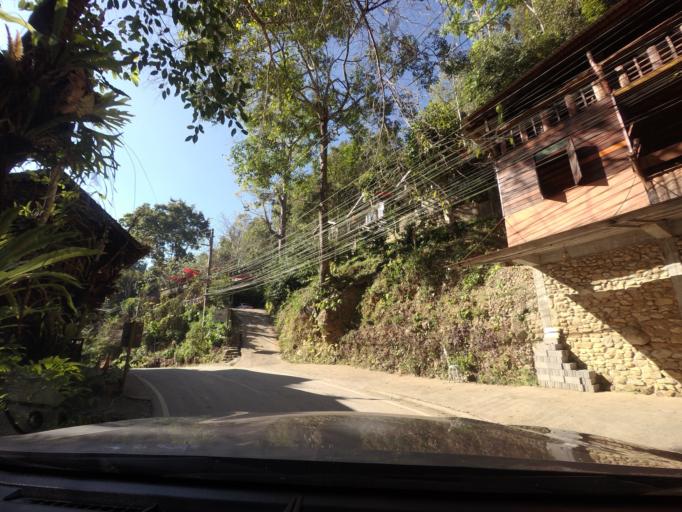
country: TH
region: Chiang Mai
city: Mae On
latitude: 18.8667
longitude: 99.3549
